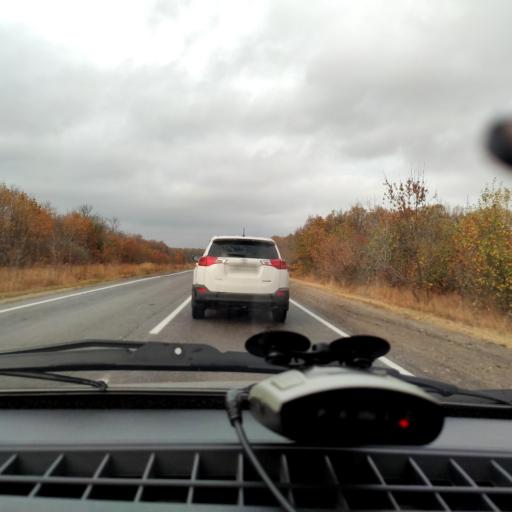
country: RU
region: Voronezj
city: Kolodeznyy
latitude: 51.3731
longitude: 39.0221
